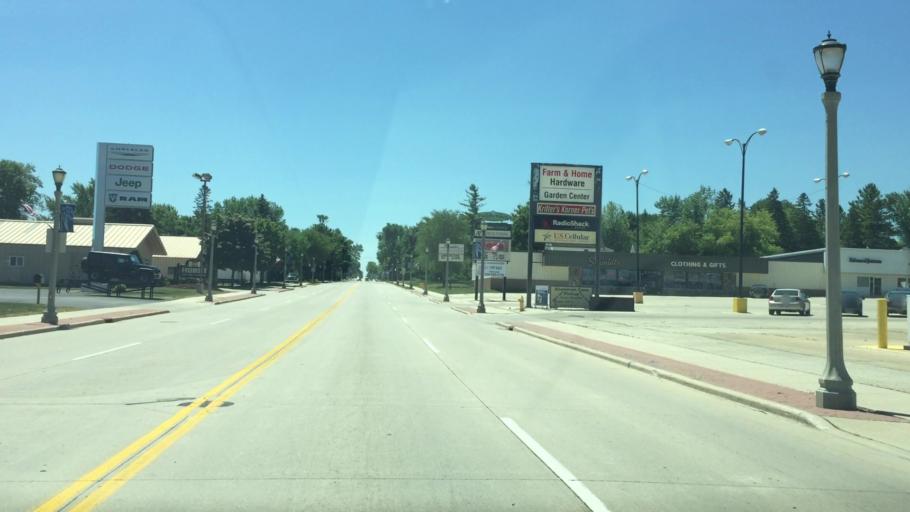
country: US
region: Wisconsin
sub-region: Calumet County
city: Chilton
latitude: 44.0359
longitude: -88.1629
